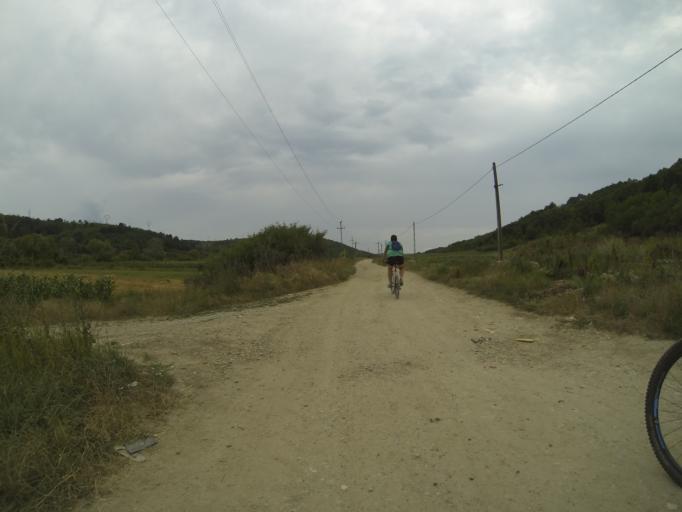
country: RO
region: Dolj
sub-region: Comuna Bradesti
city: Bradesti
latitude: 44.5024
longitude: 23.6457
